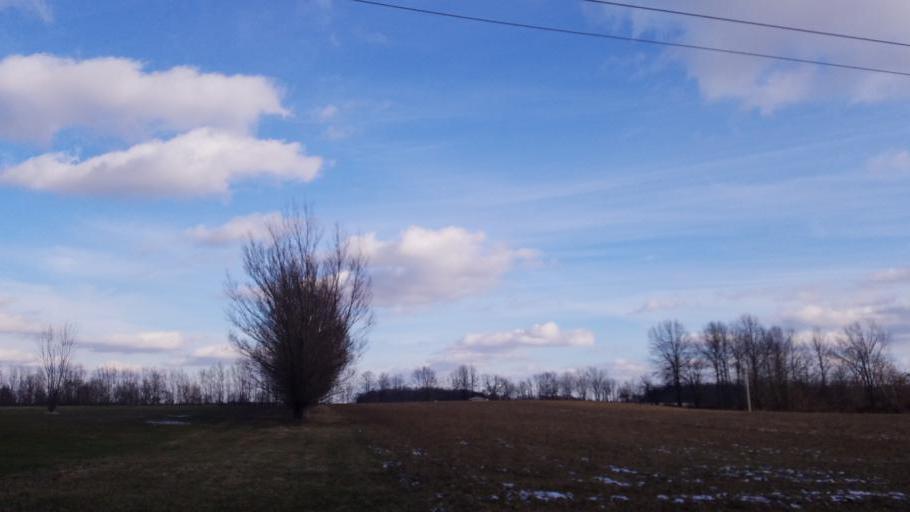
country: US
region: Ohio
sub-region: Crawford County
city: Galion
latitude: 40.6562
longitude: -82.7185
